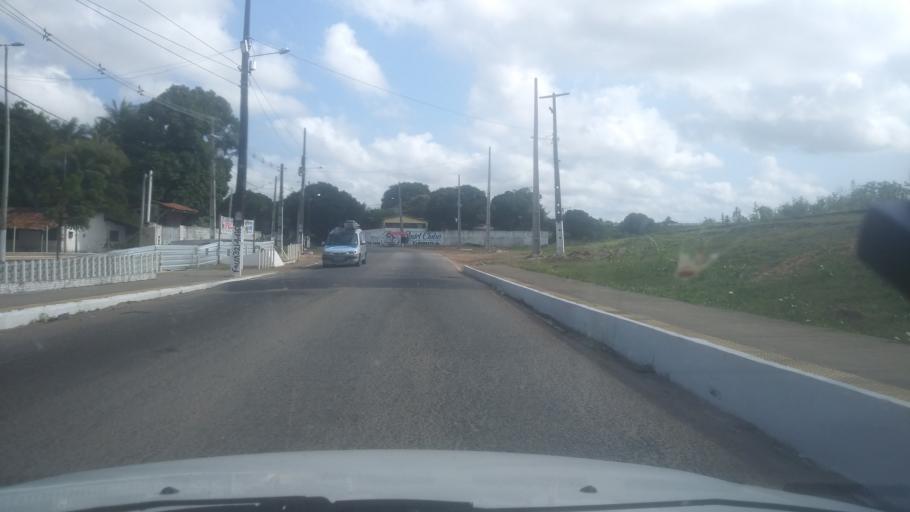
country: BR
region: Rio Grande do Norte
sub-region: Extremoz
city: Extremoz
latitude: -5.7055
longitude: -35.2815
